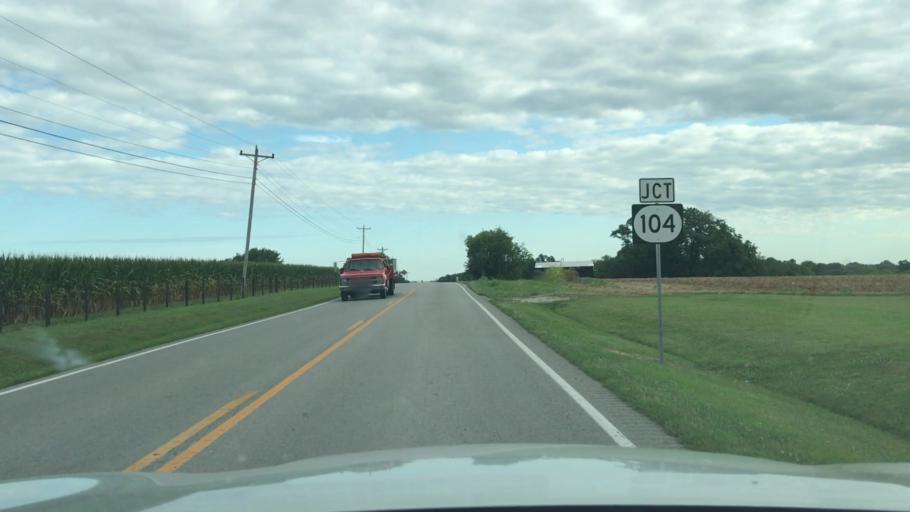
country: US
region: Kentucky
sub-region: Todd County
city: Elkton
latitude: 36.7856
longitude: -87.1638
